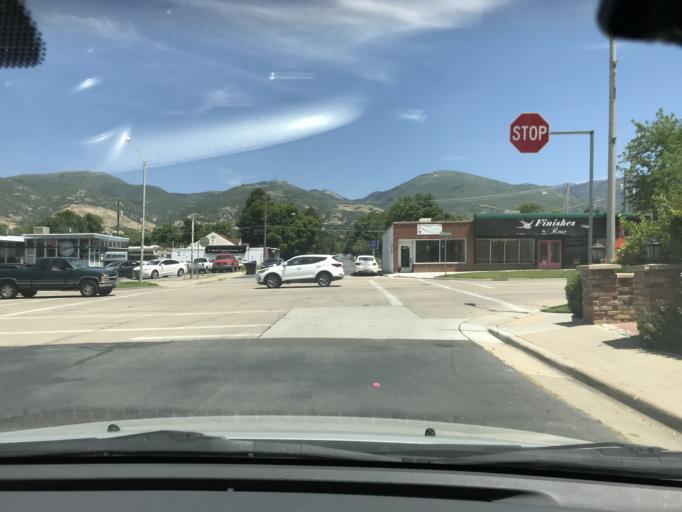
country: US
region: Utah
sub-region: Davis County
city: Bountiful
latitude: 40.8852
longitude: -111.8810
